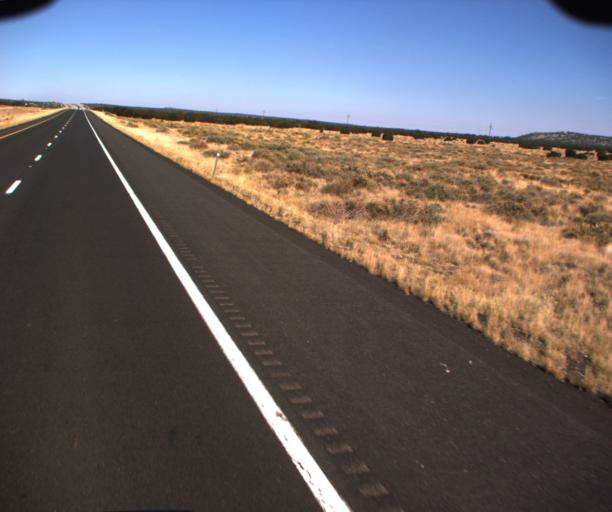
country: US
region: Arizona
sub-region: Coconino County
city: Flagstaff
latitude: 35.4475
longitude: -111.5637
